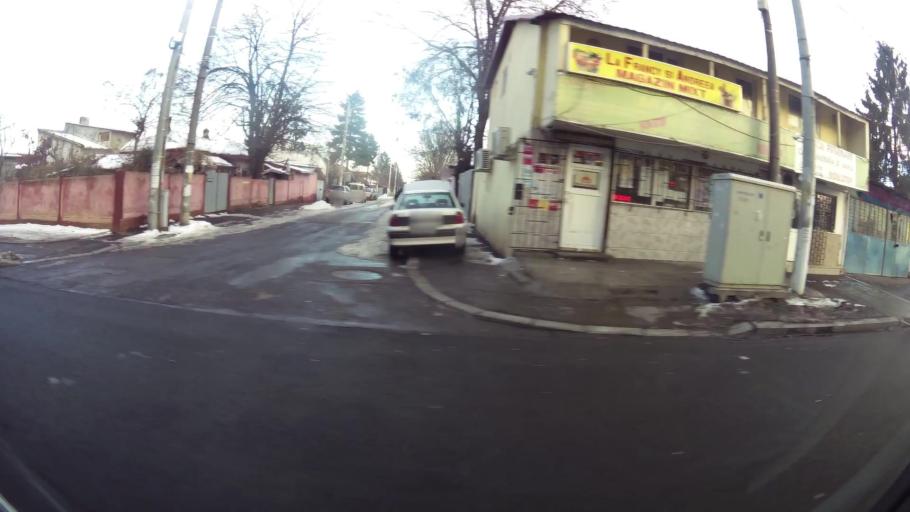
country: RO
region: Bucuresti
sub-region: Municipiul Bucuresti
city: Bucuresti
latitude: 44.3932
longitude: 26.0701
